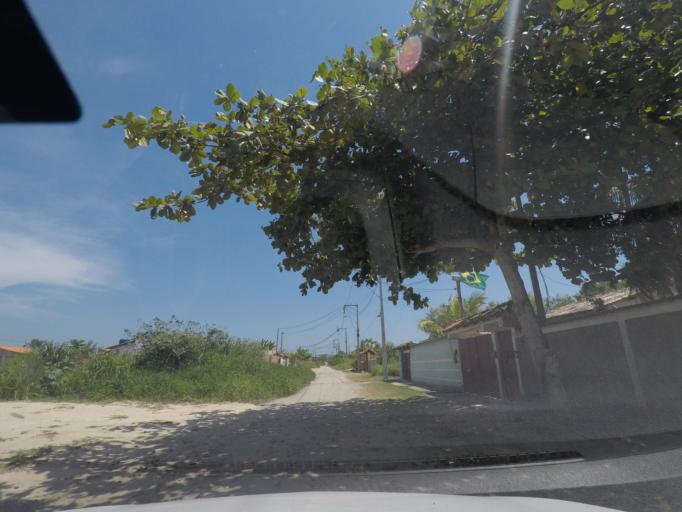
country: BR
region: Rio de Janeiro
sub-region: Marica
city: Marica
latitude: -22.9602
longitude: -42.9541
